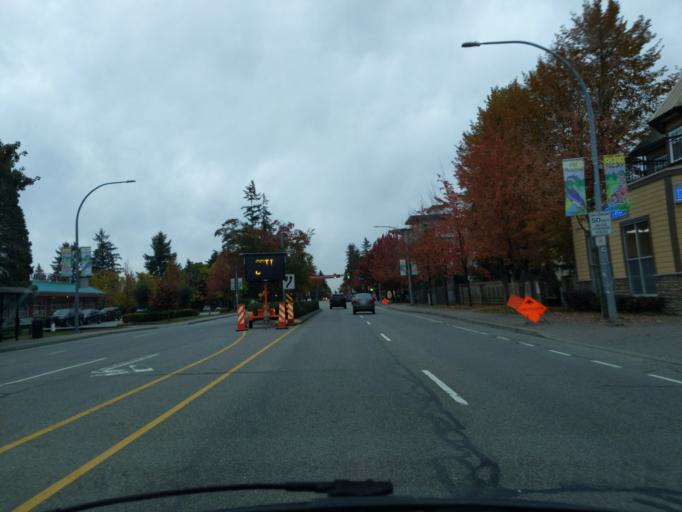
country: CA
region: British Columbia
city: Pitt Meadows
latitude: 49.2292
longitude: -122.6896
